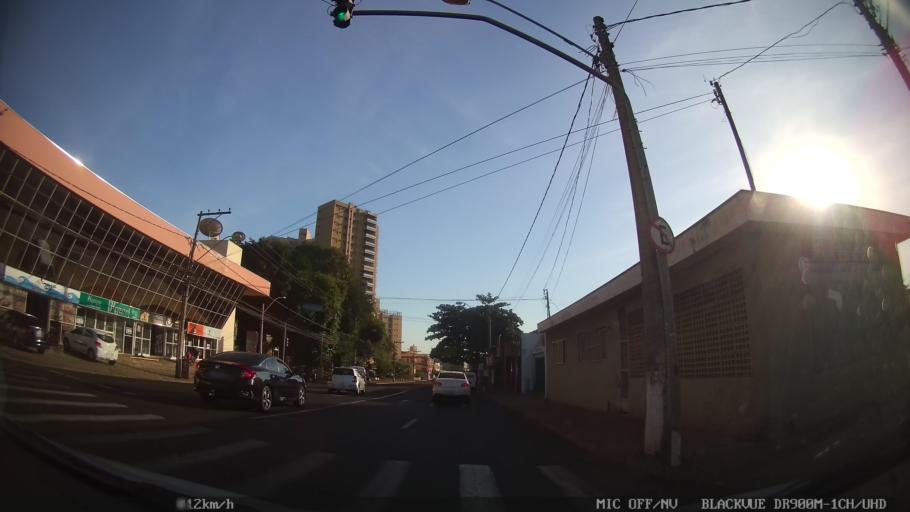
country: BR
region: Sao Paulo
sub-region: Ribeirao Preto
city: Ribeirao Preto
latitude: -21.1898
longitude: -47.8012
